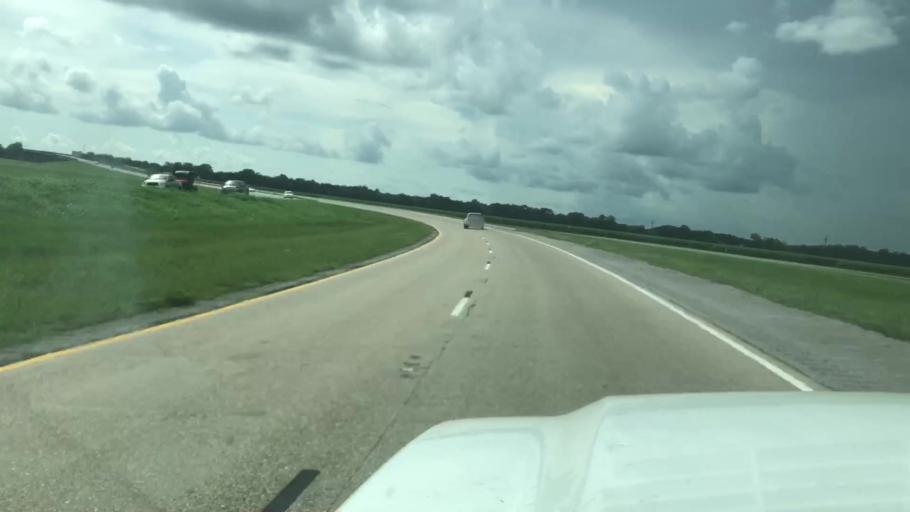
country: US
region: Louisiana
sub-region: Saint Mary Parish
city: Franklin
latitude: 29.7577
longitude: -91.4570
